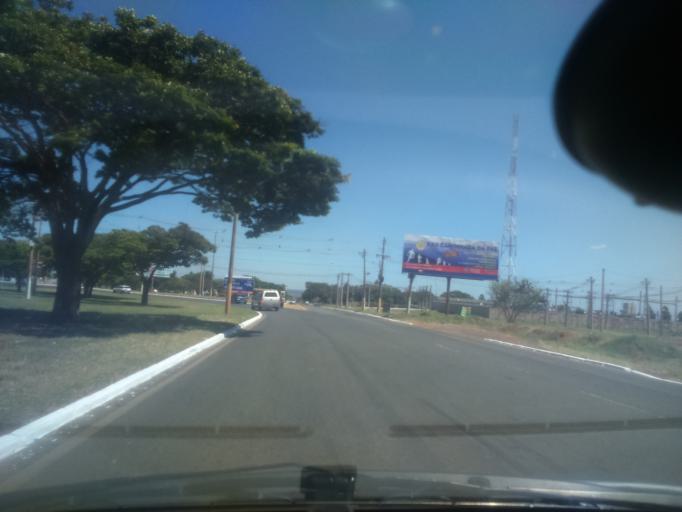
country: BR
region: Federal District
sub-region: Brasilia
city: Brasilia
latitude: -15.9977
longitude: -48.0586
